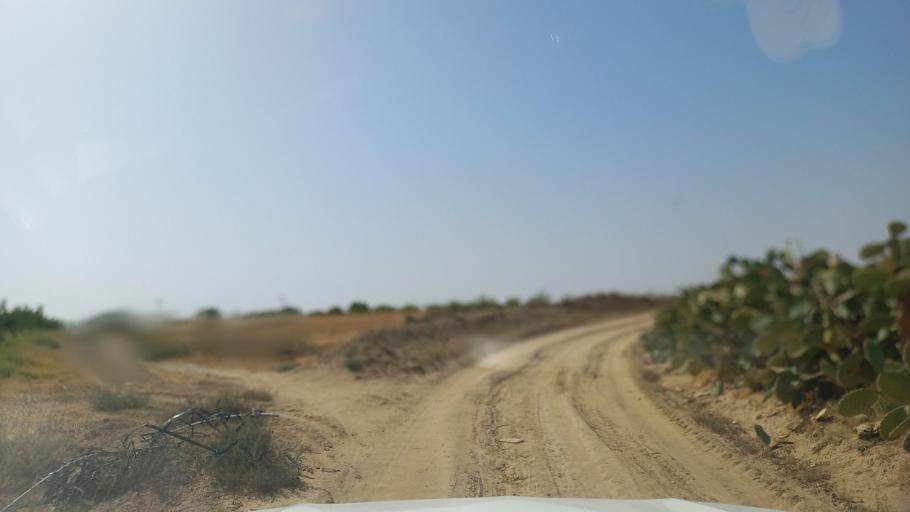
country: TN
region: Al Qasrayn
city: Kasserine
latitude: 35.2470
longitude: 9.0428
